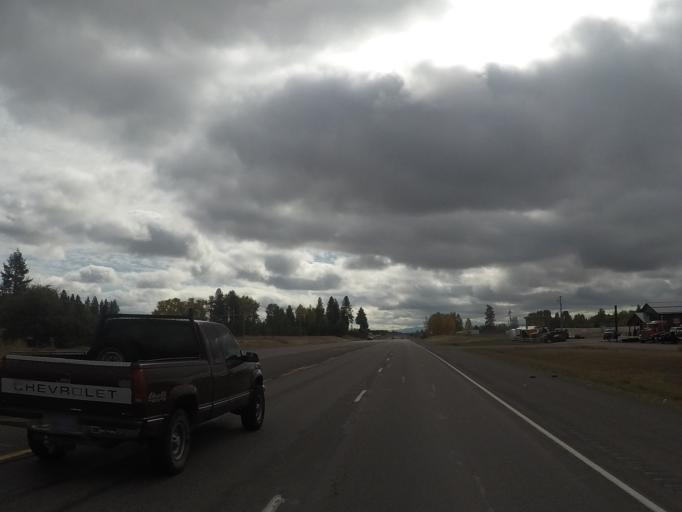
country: US
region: Montana
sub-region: Flathead County
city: Columbia Falls
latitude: 48.3612
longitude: -114.2411
